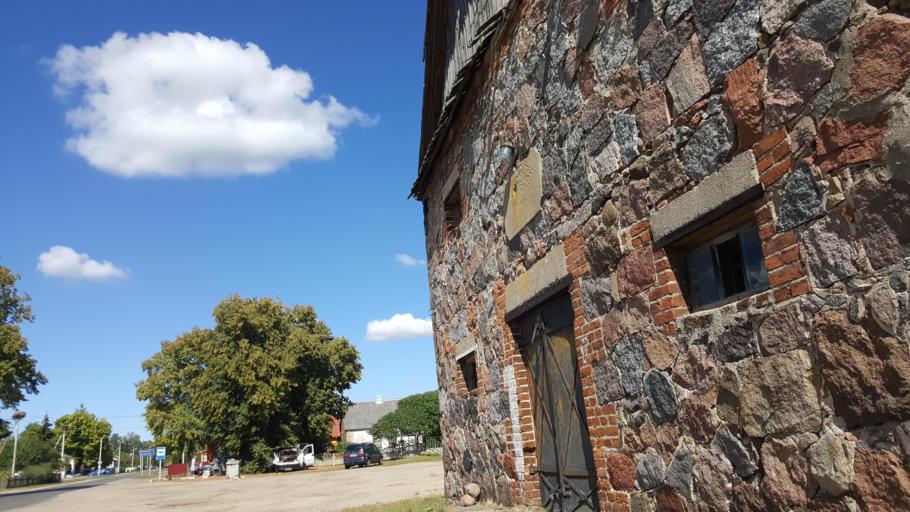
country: BY
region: Brest
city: Vysokaye
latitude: 52.2812
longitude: 23.3129
